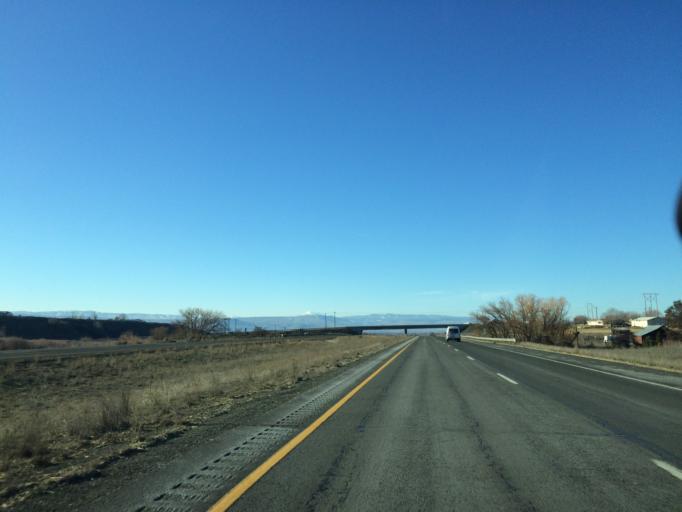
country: US
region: Washington
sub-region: Kittitas County
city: Kittitas
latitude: 46.9722
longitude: -120.3577
